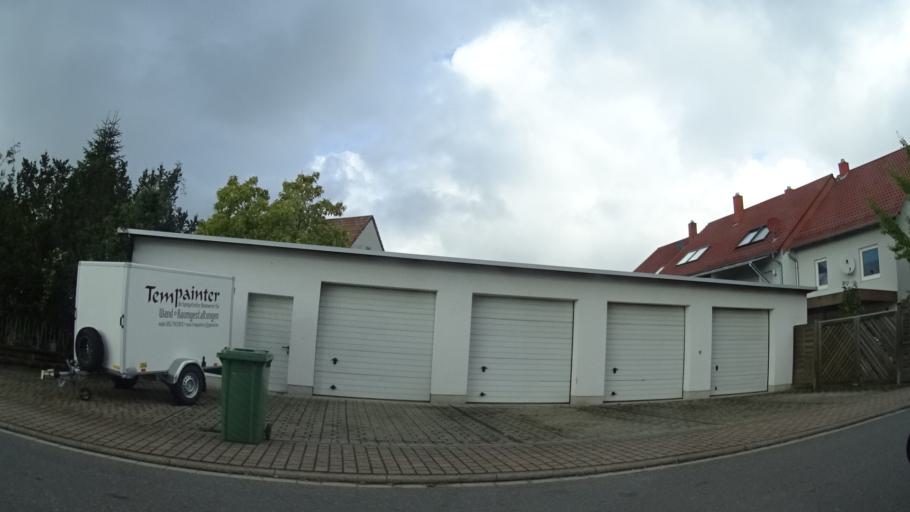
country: DE
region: Baden-Wuerttemberg
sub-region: Karlsruhe Region
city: Malsch
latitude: 49.2474
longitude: 8.6869
